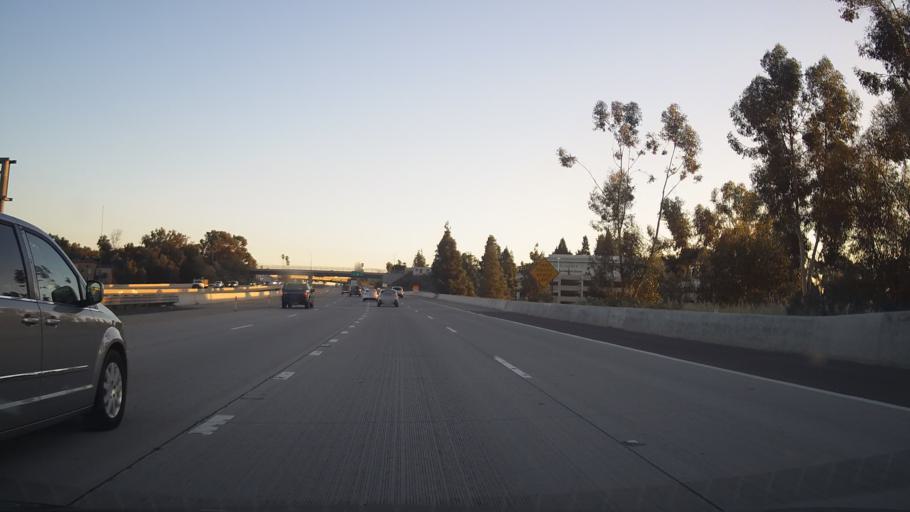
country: US
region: California
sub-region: San Diego County
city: La Mesa
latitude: 32.7858
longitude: -117.0064
